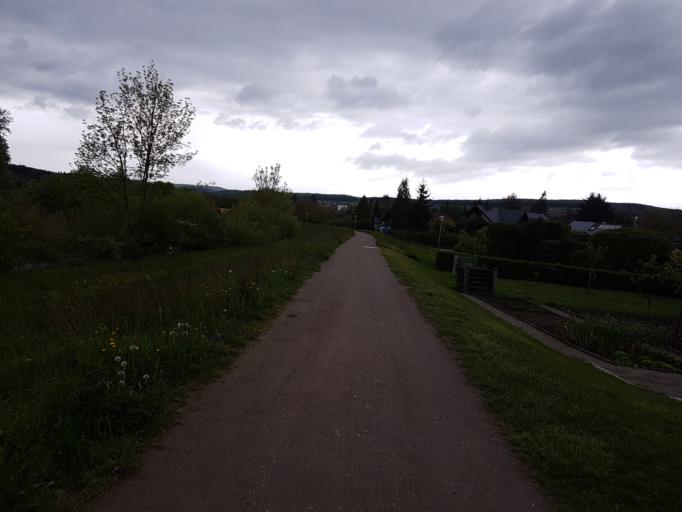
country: DE
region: Baden-Wuerttemberg
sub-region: Freiburg Region
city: Lauchringen
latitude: 47.6248
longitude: 8.3198
